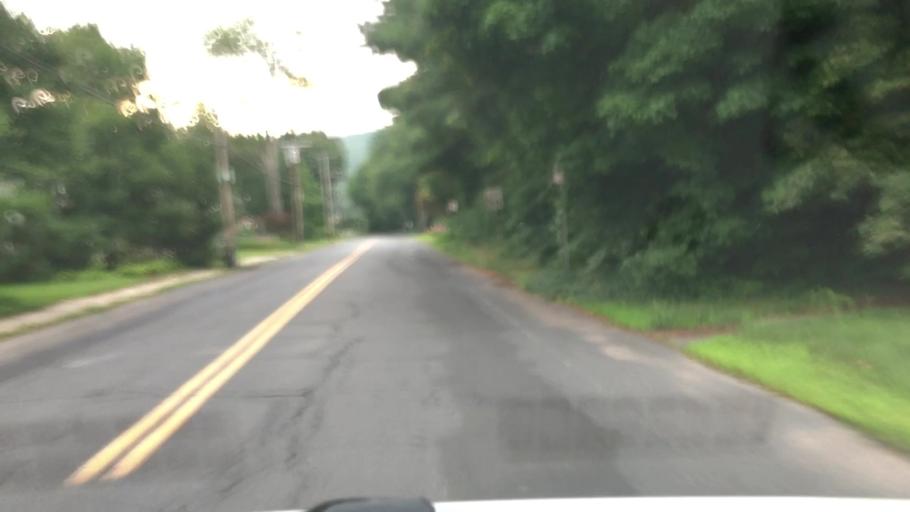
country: US
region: Massachusetts
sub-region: Hampshire County
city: Easthampton
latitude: 42.2725
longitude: -72.6494
